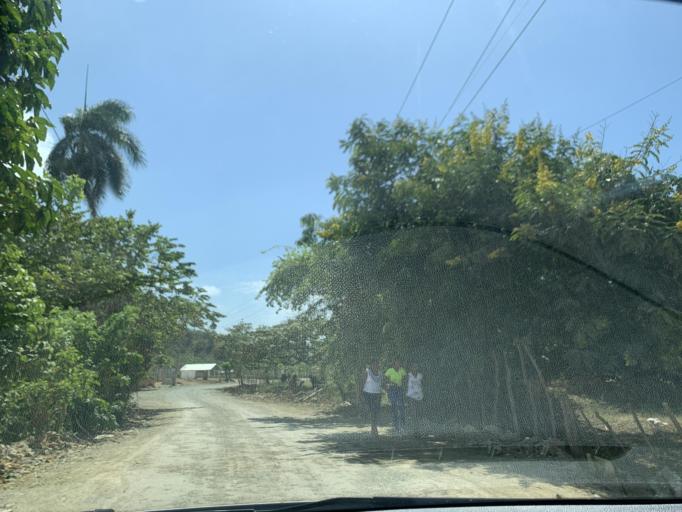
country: DO
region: Puerto Plata
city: Luperon
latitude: 19.8817
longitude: -70.8417
